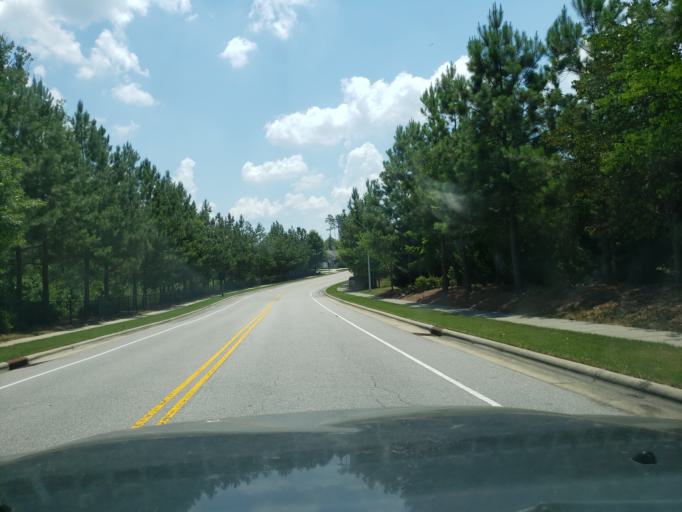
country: US
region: North Carolina
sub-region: Wake County
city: Green Level
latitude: 35.8385
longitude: -78.9132
